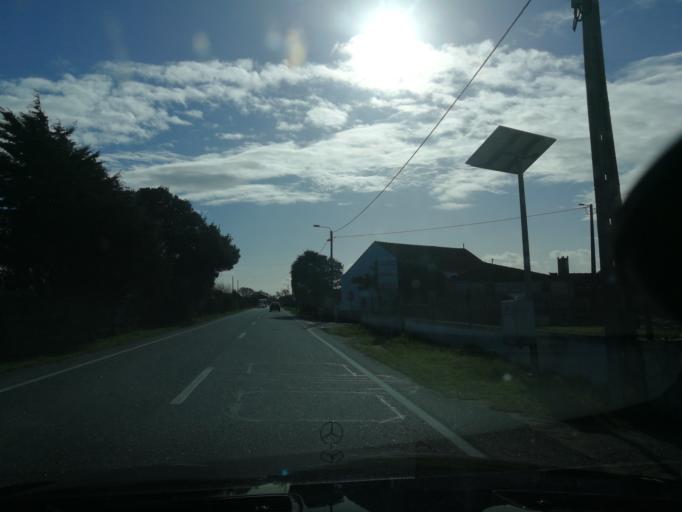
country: PT
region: Aveiro
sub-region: Estarreja
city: Pardilho
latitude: 40.8243
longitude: -8.6674
